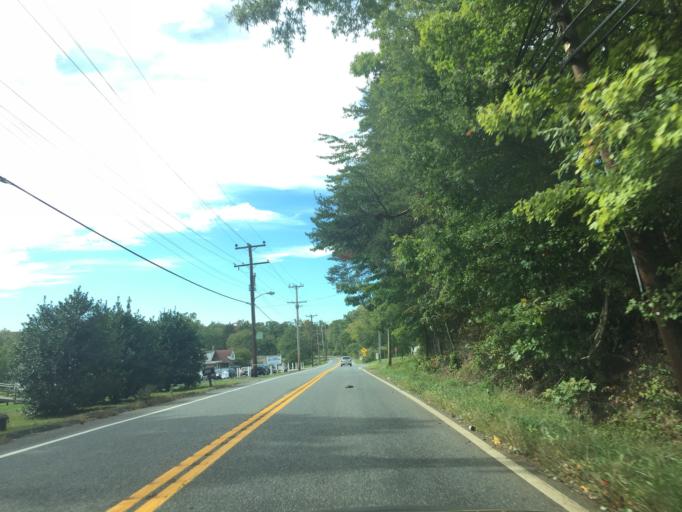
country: US
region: Maryland
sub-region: Harford County
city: Joppatowne
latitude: 39.4304
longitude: -76.3691
